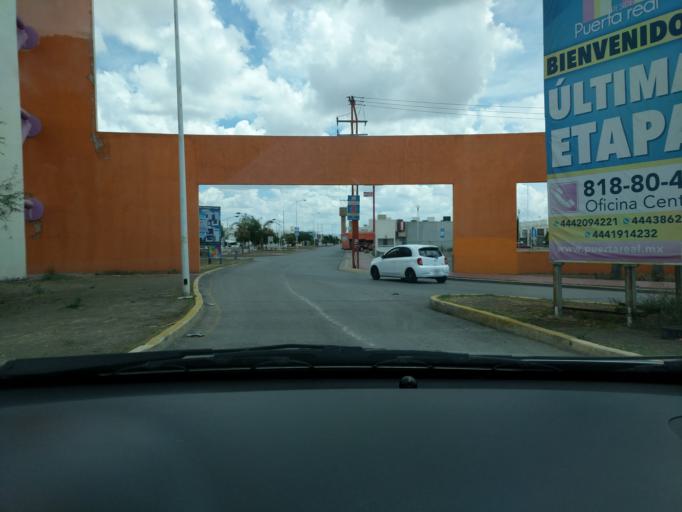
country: MX
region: San Luis Potosi
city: Soledad Diez Gutierrez
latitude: 22.2138
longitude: -100.9380
